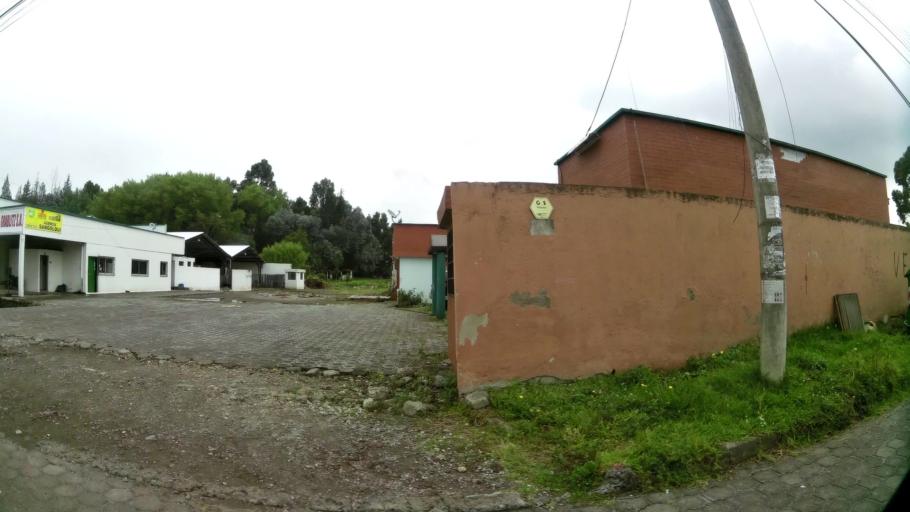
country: EC
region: Pichincha
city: Sangolqui
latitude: -0.3235
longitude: -78.4396
